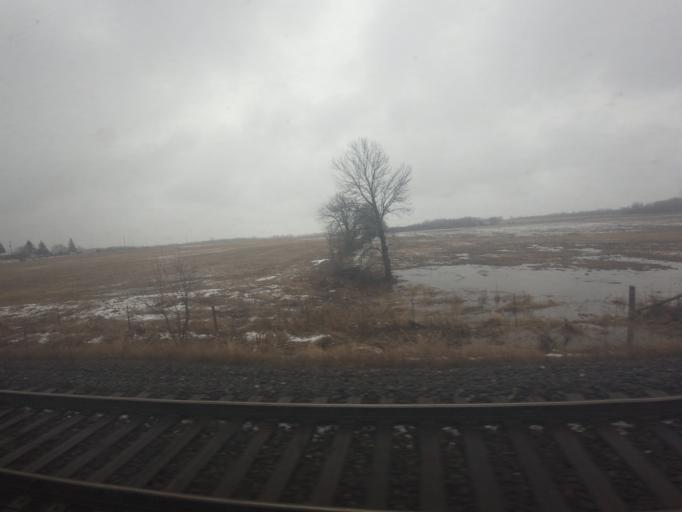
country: CA
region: Ontario
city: Belleville
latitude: 44.1998
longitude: -77.2929
